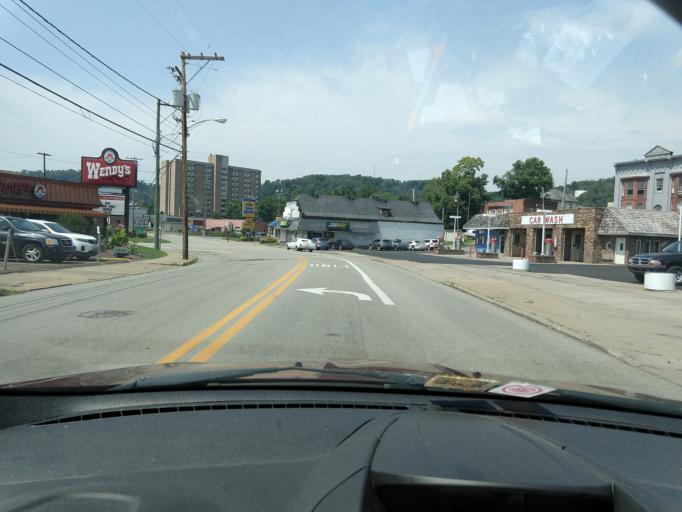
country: US
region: West Virginia
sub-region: Harrison County
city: Clarksburg
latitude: 39.2824
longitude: -80.3502
